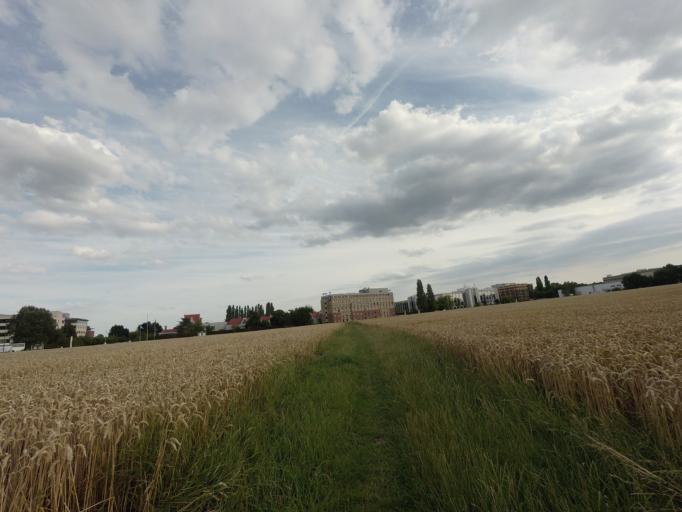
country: BE
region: Flanders
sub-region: Provincie Vlaams-Brabant
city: Diegem
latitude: 50.8839
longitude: 4.4370
